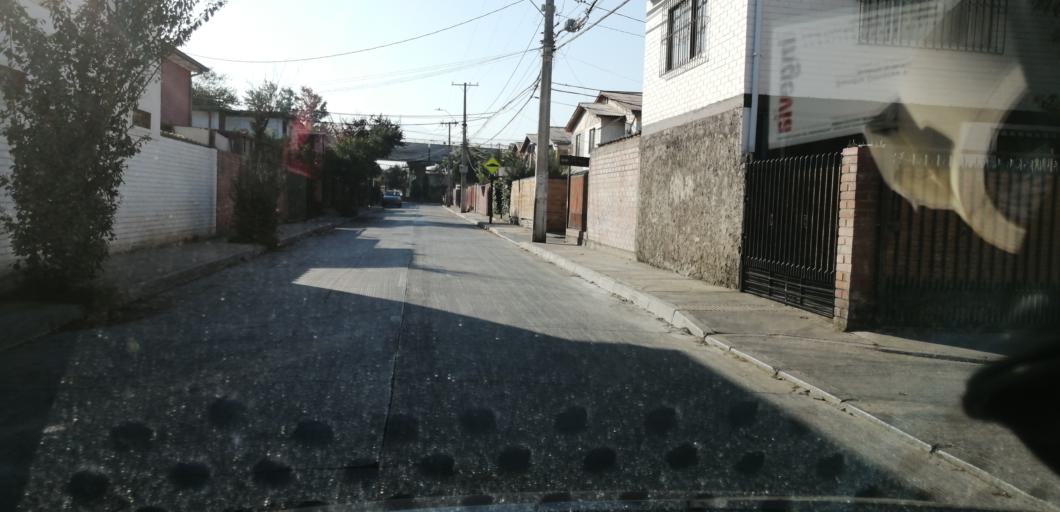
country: CL
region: Santiago Metropolitan
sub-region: Provincia de Santiago
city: Lo Prado
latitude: -33.4590
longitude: -70.7396
